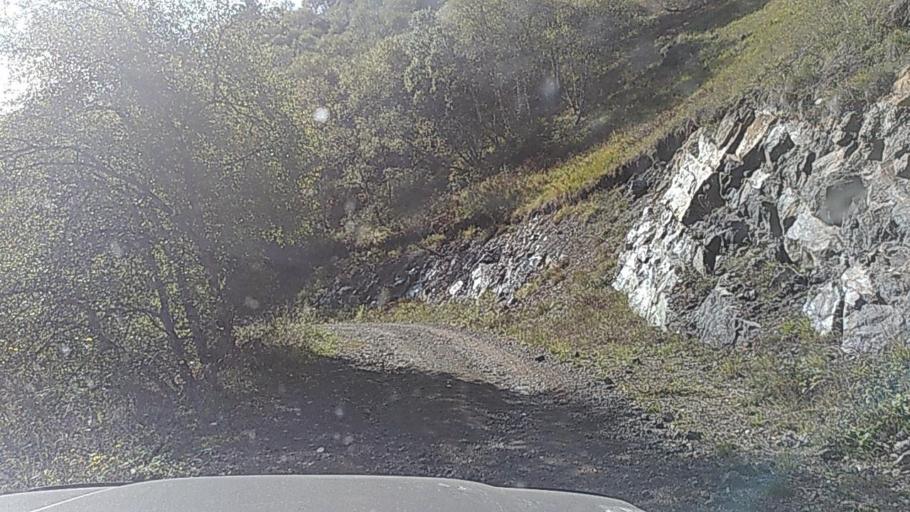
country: RU
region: Kabardino-Balkariya
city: Kamennomostskoye
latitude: 43.7157
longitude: 42.8455
